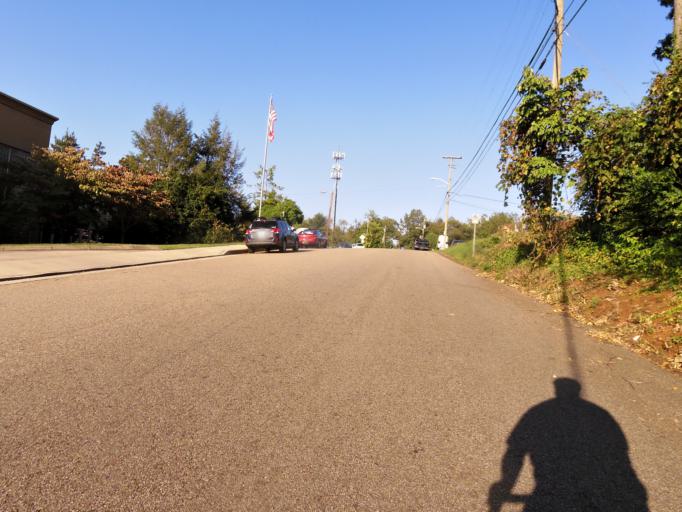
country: US
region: Tennessee
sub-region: Knox County
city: Knoxville
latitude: 35.9982
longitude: -83.9228
